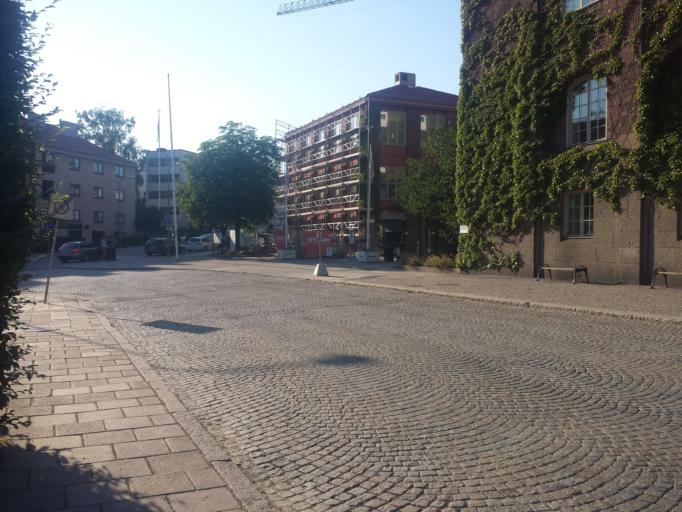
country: SE
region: Stockholm
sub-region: Stockholms Kommun
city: OEstermalm
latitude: 59.3466
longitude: 18.0728
